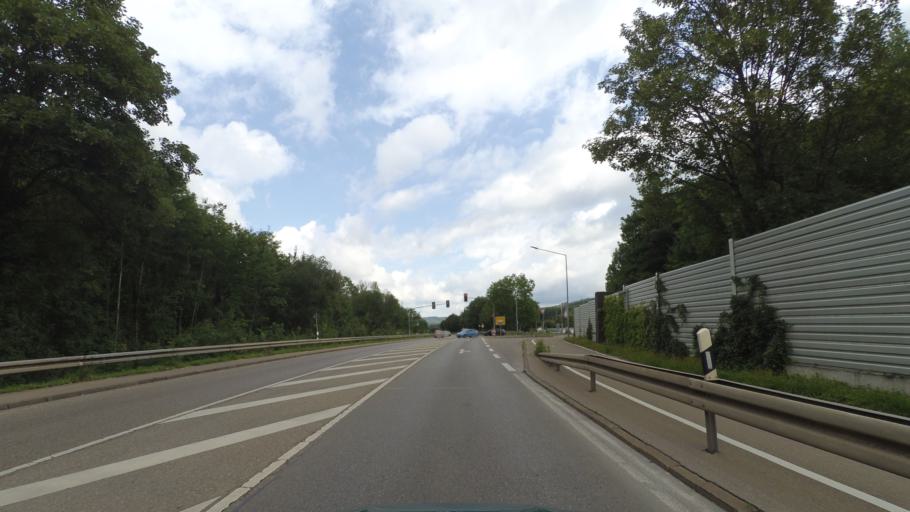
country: DE
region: Baden-Wuerttemberg
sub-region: Regierungsbezirk Stuttgart
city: Kuchen
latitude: 48.6432
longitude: 9.7899
